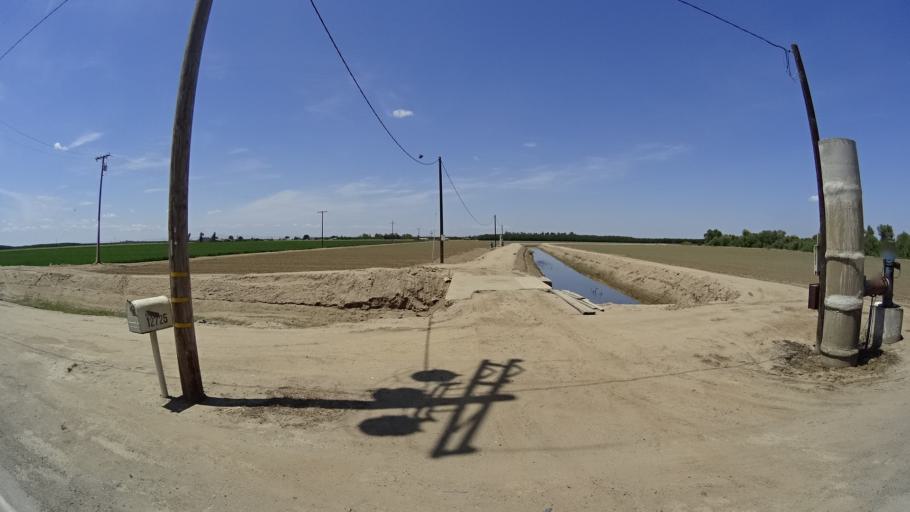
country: US
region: California
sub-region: Kings County
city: Home Garden
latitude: 36.2879
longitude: -119.6728
